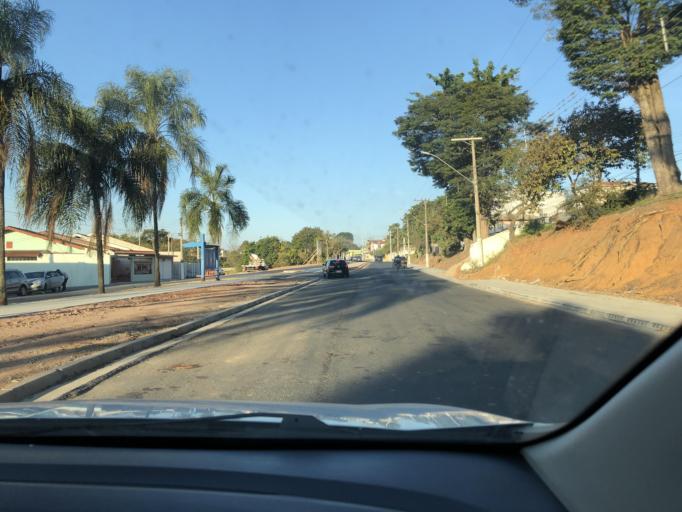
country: BR
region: Sao Paulo
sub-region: Atibaia
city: Atibaia
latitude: -23.1102
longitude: -46.5482
